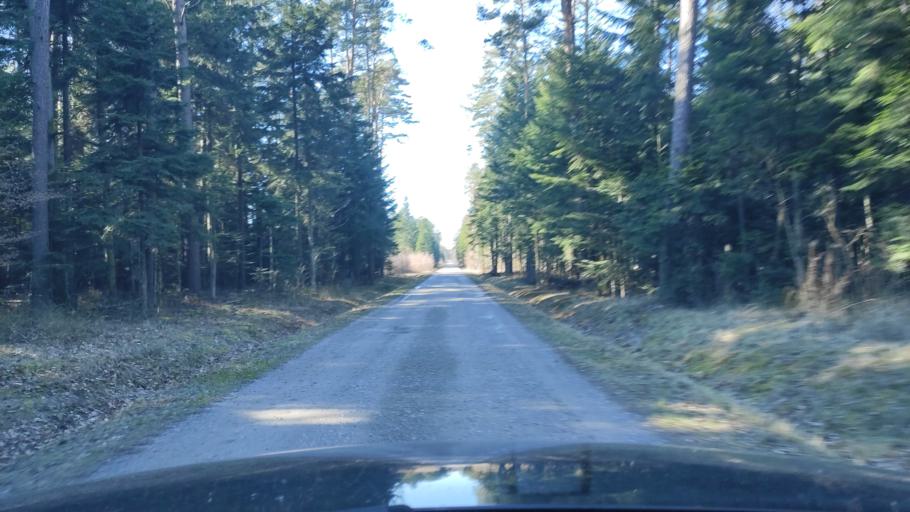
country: PL
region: Masovian Voivodeship
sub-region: Powiat radomski
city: Jedlnia-Letnisko
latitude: 51.4672
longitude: 21.3125
